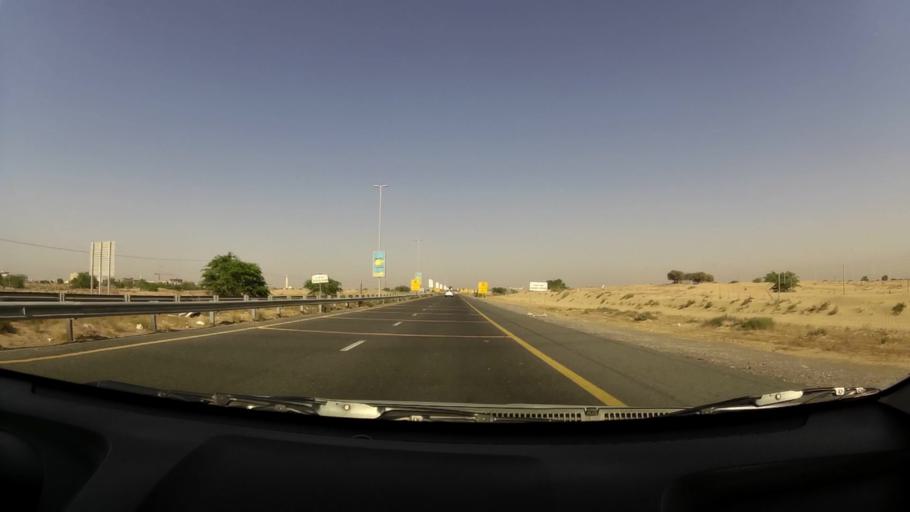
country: AE
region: Umm al Qaywayn
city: Umm al Qaywayn
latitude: 25.4709
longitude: 55.5807
